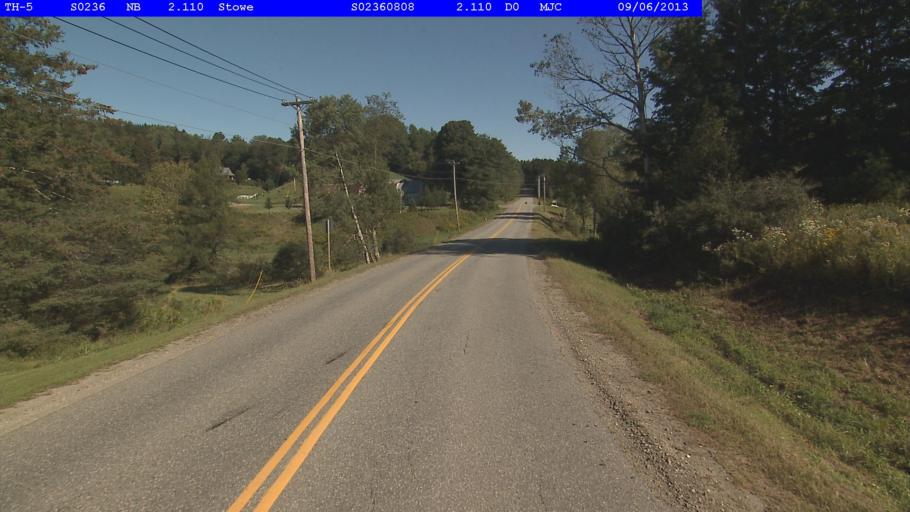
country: US
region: Vermont
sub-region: Washington County
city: Waterbury
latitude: 44.4554
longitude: -72.7296
